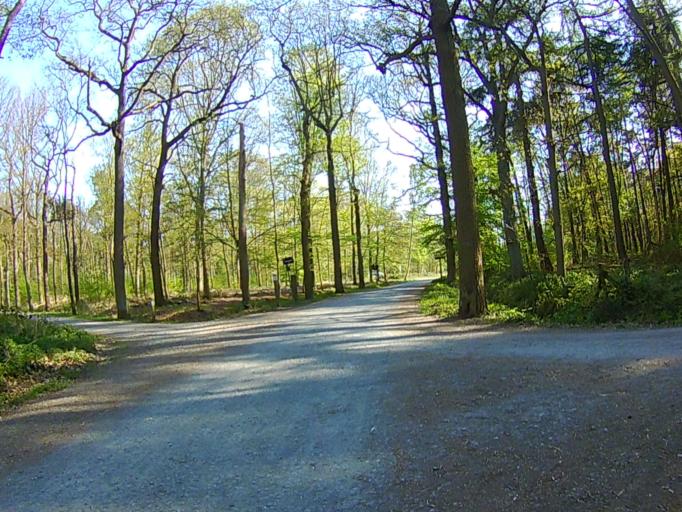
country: BE
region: Flanders
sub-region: Provincie Antwerpen
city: Brasschaat
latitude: 51.2708
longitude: 4.4850
